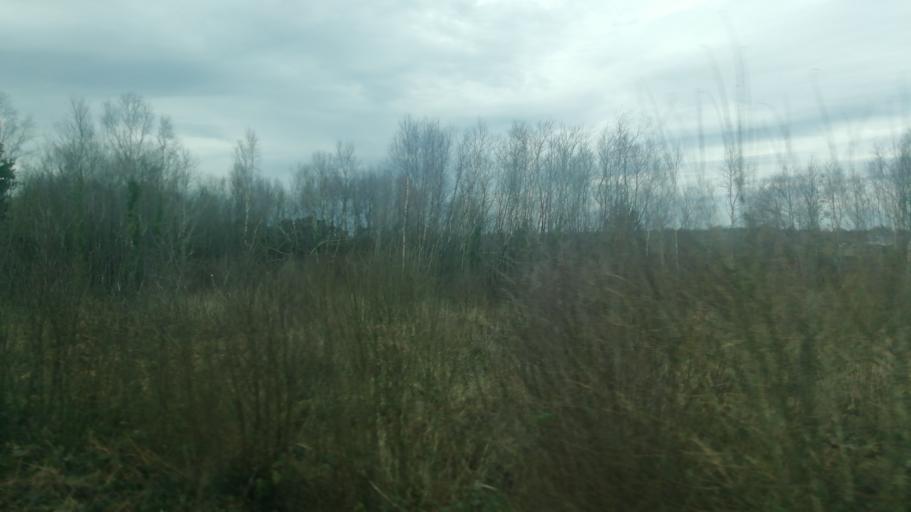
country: IE
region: Leinster
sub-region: Kildare
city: Derrinturn
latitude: 53.2822
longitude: -6.9093
